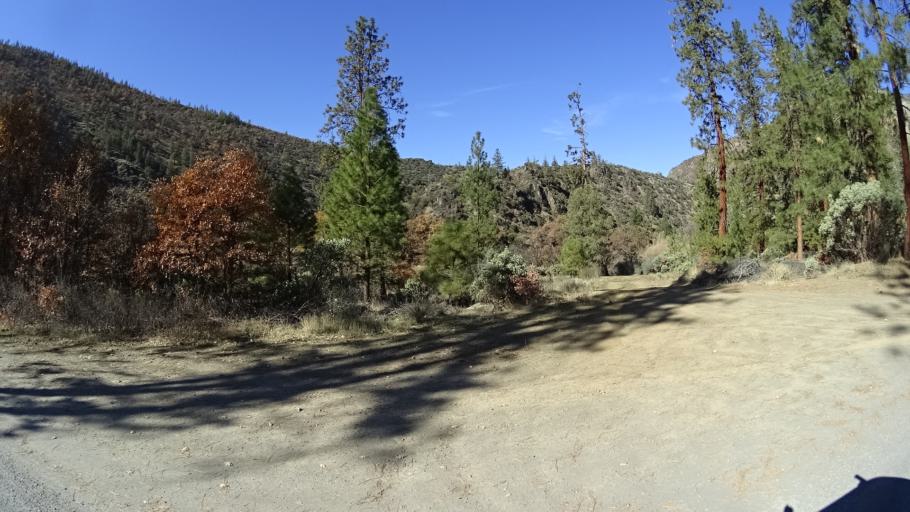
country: US
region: California
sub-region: Siskiyou County
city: Yreka
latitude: 41.8260
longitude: -122.6568
